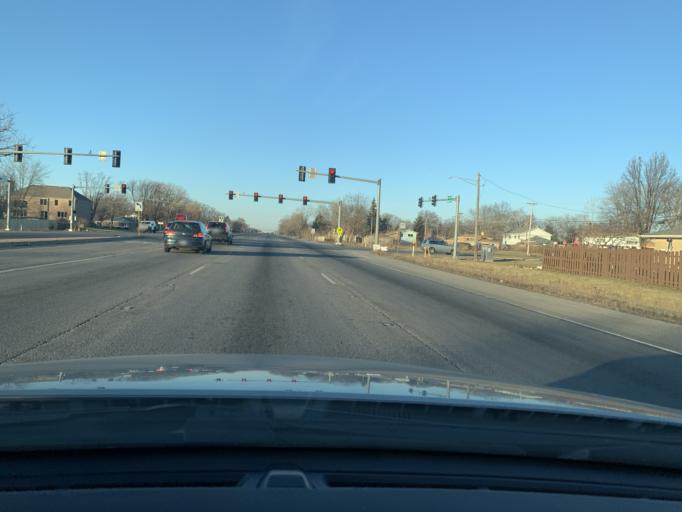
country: US
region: Illinois
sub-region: DuPage County
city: Wood Dale
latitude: 41.9640
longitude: -87.9592
